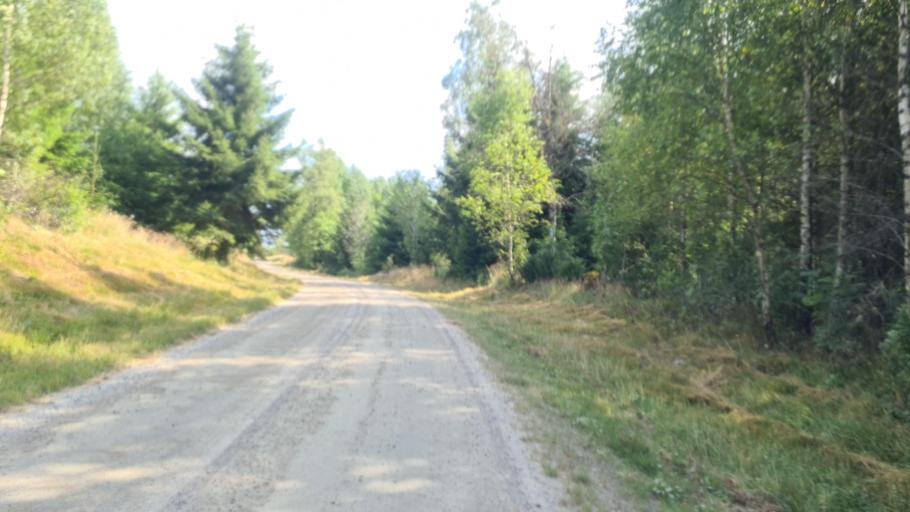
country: SE
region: Kronoberg
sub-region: Ljungby Kommun
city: Ljungby
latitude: 56.7255
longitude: 13.8845
